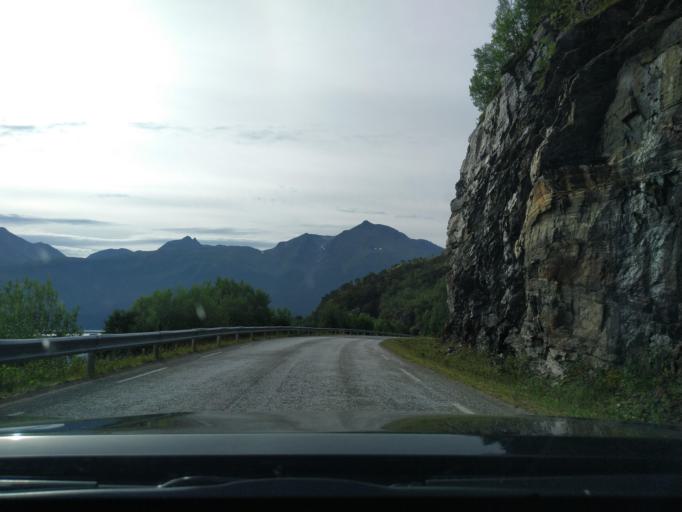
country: NO
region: Troms
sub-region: Dyroy
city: Brostadbotn
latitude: 68.8822
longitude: 17.4719
